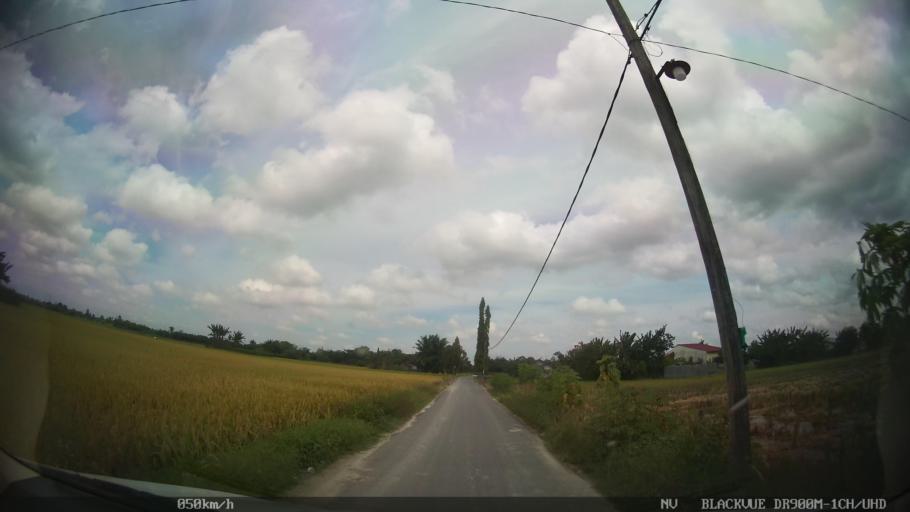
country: ID
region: North Sumatra
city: Percut
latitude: 3.5720
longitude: 98.8489
